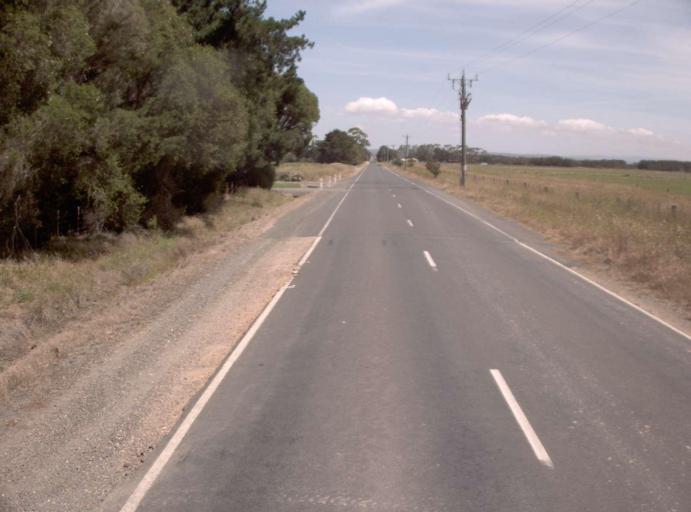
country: AU
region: Victoria
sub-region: Wellington
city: Heyfield
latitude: -38.0795
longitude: 146.8688
